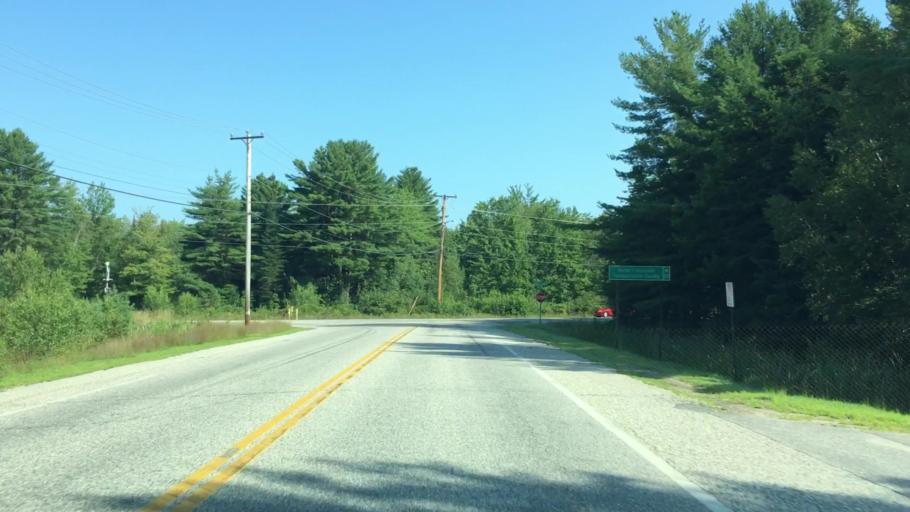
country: US
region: Maine
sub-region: Androscoggin County
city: Minot
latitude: 44.0469
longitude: -70.2957
